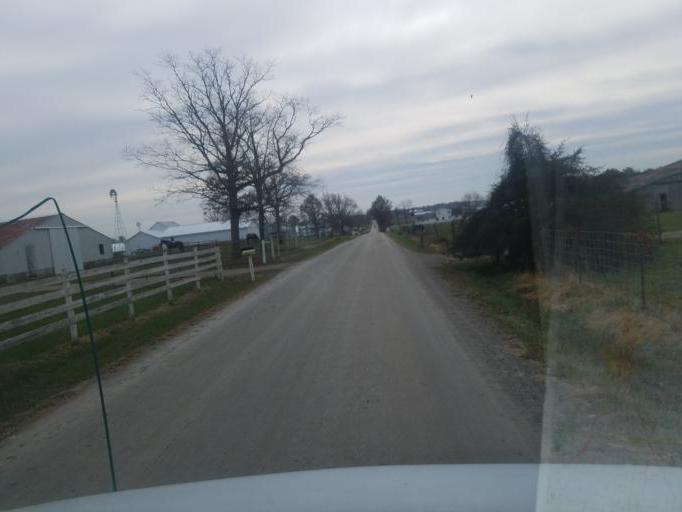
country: US
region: Indiana
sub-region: Adams County
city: Geneva
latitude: 40.6139
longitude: -84.8925
